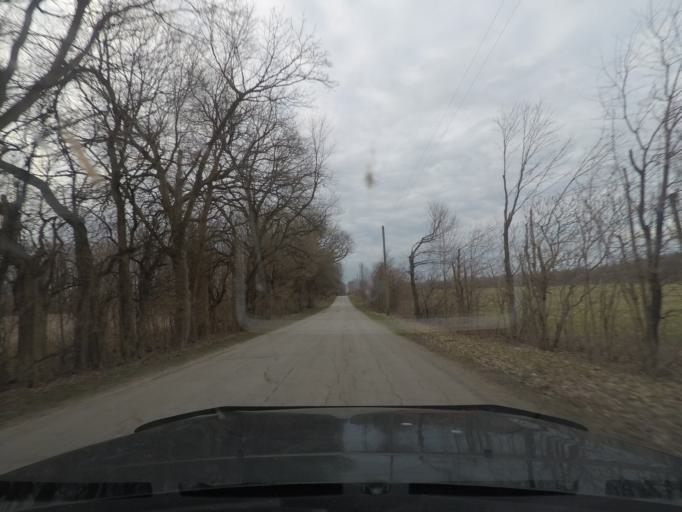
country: US
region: Indiana
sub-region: LaPorte County
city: Westville
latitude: 41.5314
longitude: -86.7989
